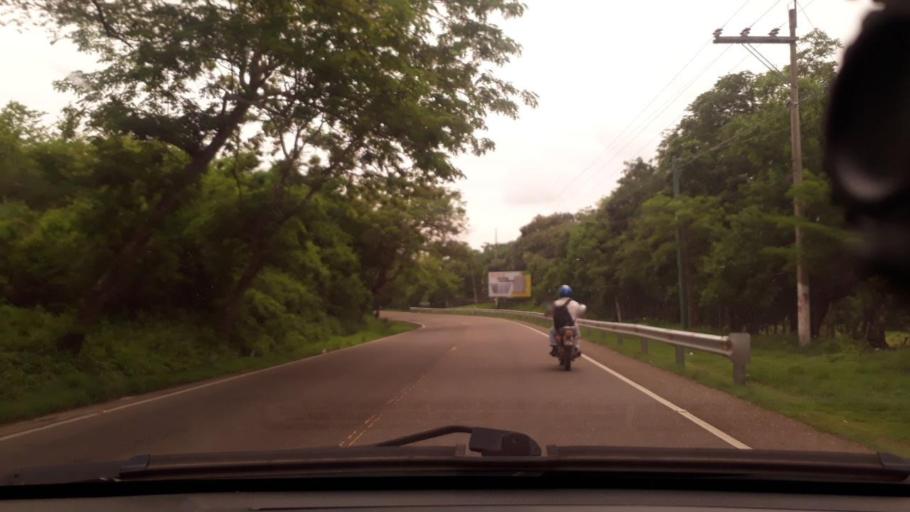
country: GT
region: Chiquimula
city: San Jacinto
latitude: 14.7258
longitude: -89.4987
